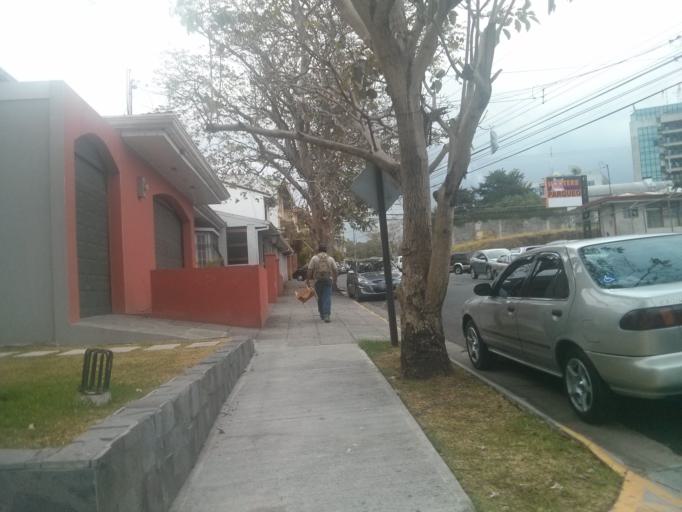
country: CR
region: San Jose
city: San Pedro
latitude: 9.9369
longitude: -84.0567
